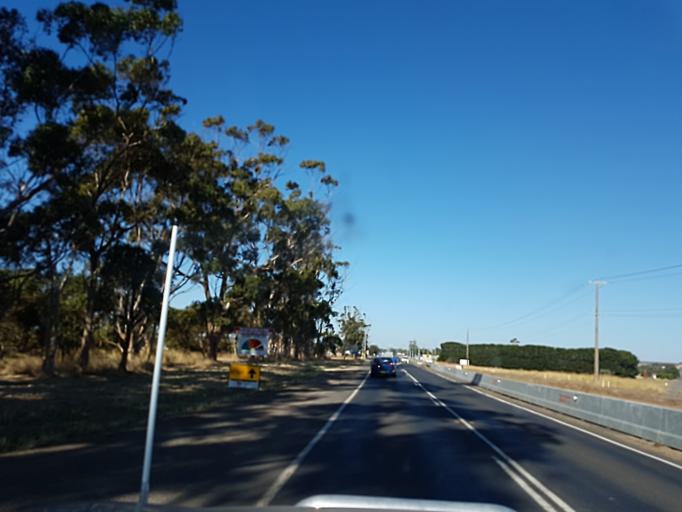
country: AU
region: Victoria
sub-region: Surf Coast
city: Anglesea
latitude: -38.2467
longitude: 143.9780
